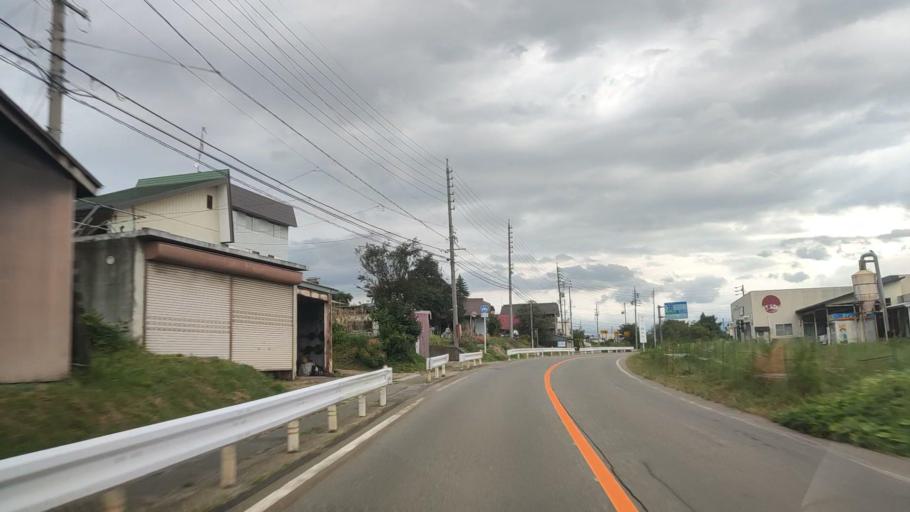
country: JP
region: Nagano
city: Iiyama
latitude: 36.8210
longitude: 138.3493
